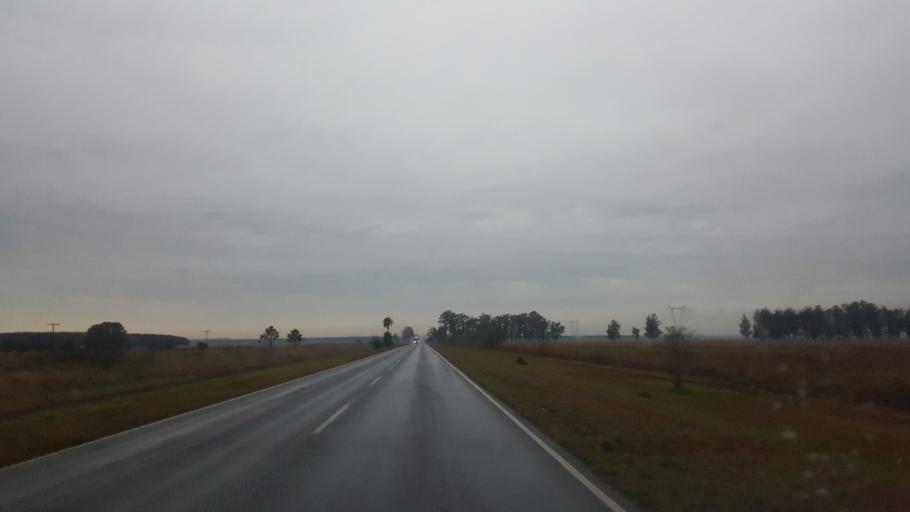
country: PY
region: Itapua
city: San Cosme y Damian
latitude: -27.5443
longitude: -56.2114
